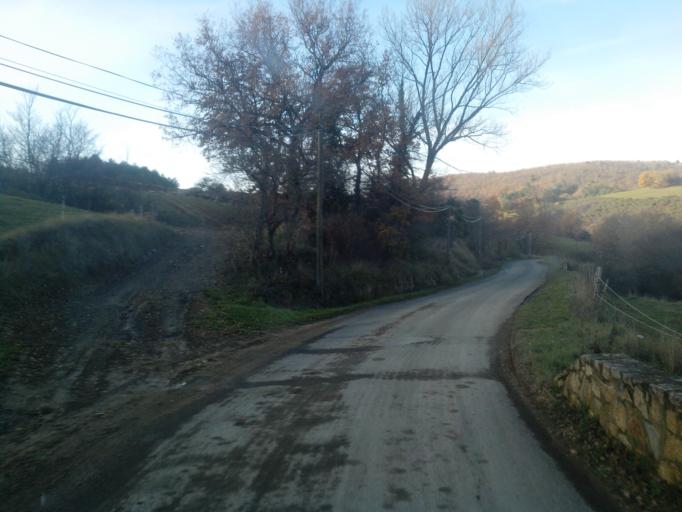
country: FR
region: Languedoc-Roussillon
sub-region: Departement de l'Aude
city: Couiza
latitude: 42.8901
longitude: 2.3161
